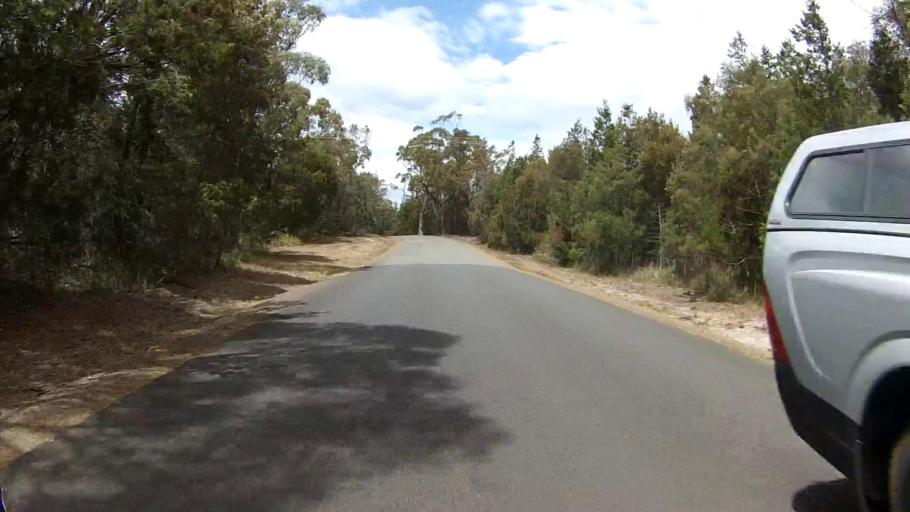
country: AU
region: Tasmania
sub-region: Sorell
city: Sorell
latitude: -42.5763
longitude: 147.9023
